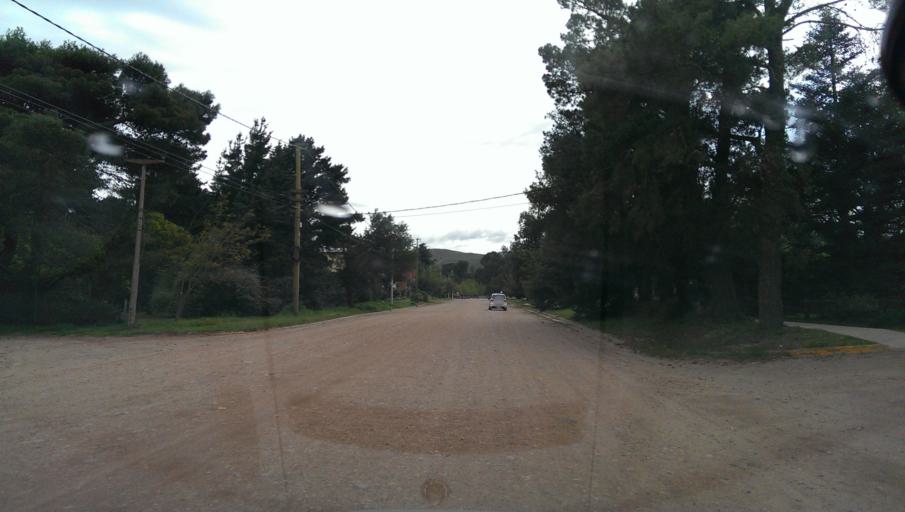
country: AR
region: Buenos Aires
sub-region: Partido de Tornquist
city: Tornquist
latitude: -38.0812
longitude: -61.9295
